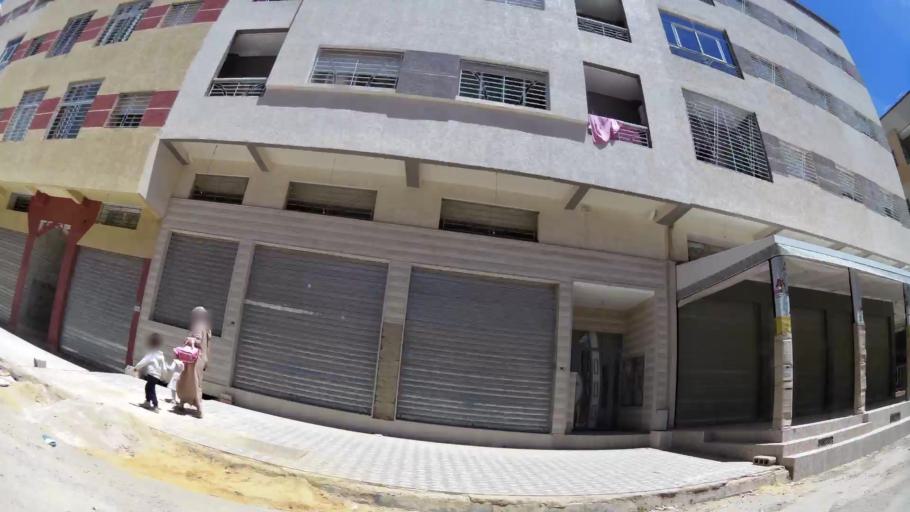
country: MA
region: Meknes-Tafilalet
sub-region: Meknes
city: Meknes
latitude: 33.8549
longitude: -5.5646
